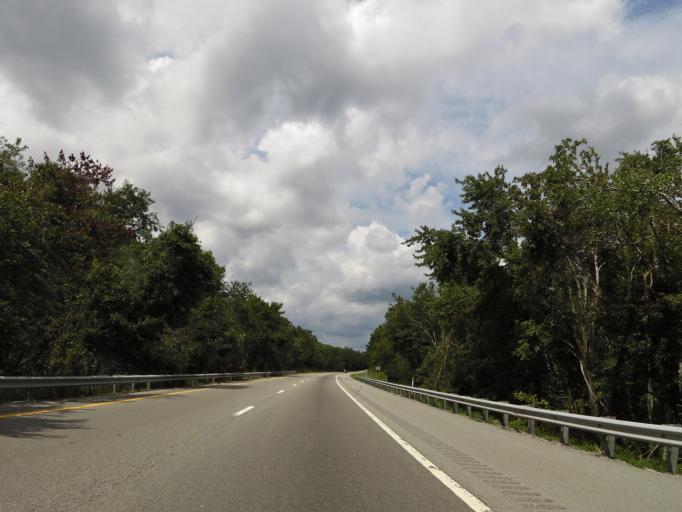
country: US
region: Tennessee
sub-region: Putnam County
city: Monterey
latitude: 36.0560
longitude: -85.1760
